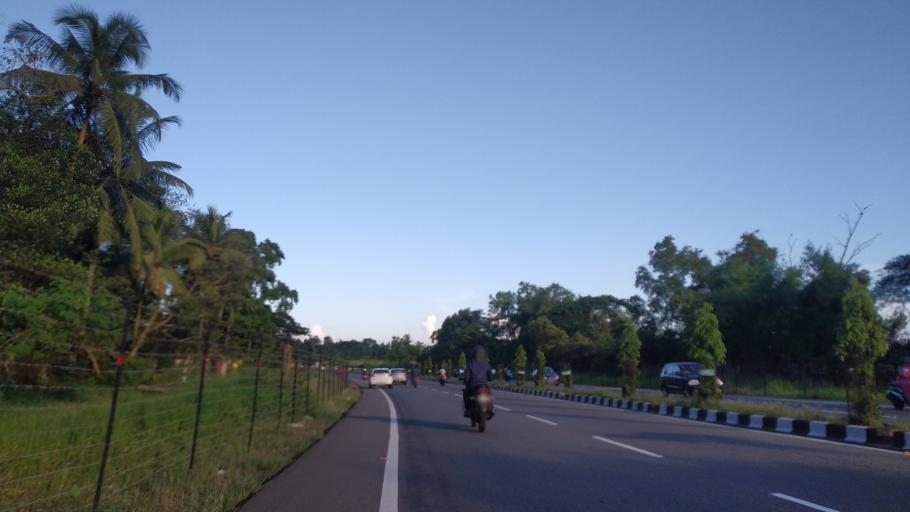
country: IN
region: Kerala
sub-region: Ernakulam
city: Elur
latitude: 10.0686
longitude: 76.3093
